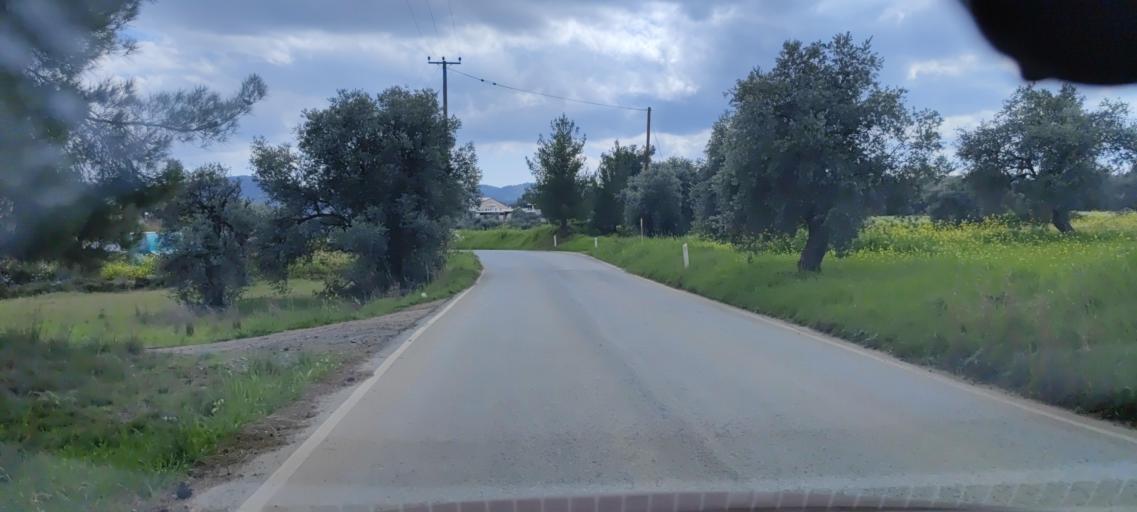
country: CY
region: Lefkosia
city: Lythrodontas
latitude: 34.9644
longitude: 33.2927
